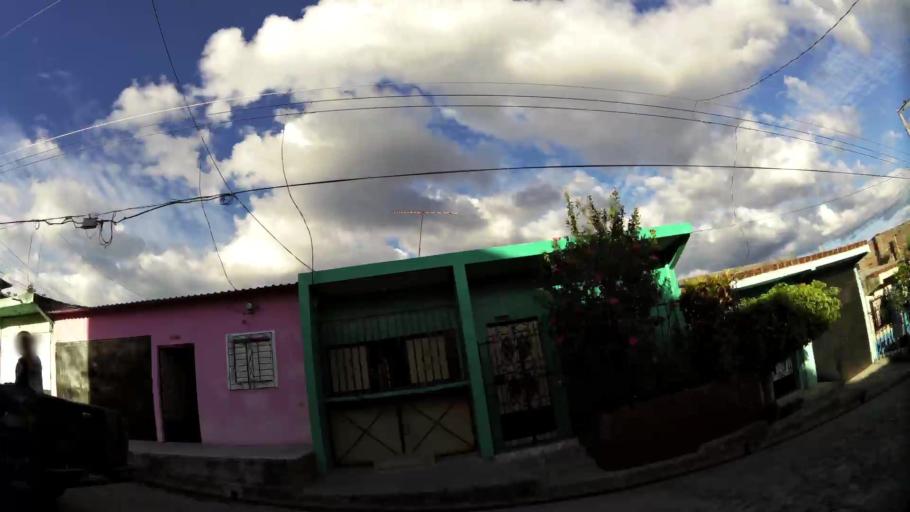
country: SV
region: Cuscatlan
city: Cojutepeque
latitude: 13.7124
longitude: -88.9290
